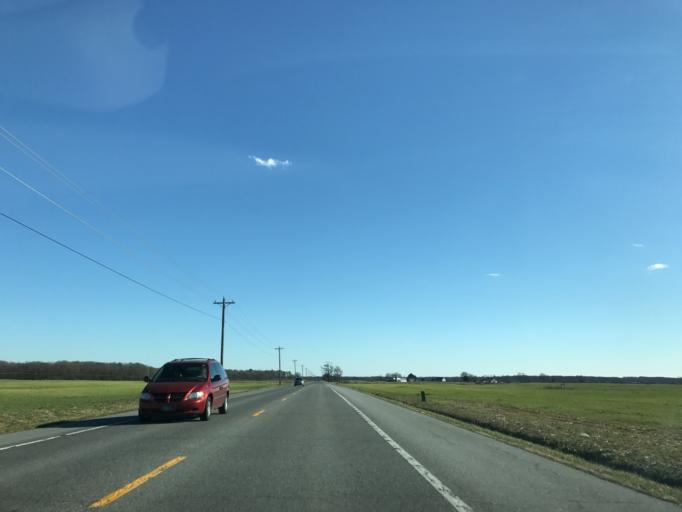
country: US
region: Maryland
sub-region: Caroline County
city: Greensboro
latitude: 39.0839
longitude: -75.8640
